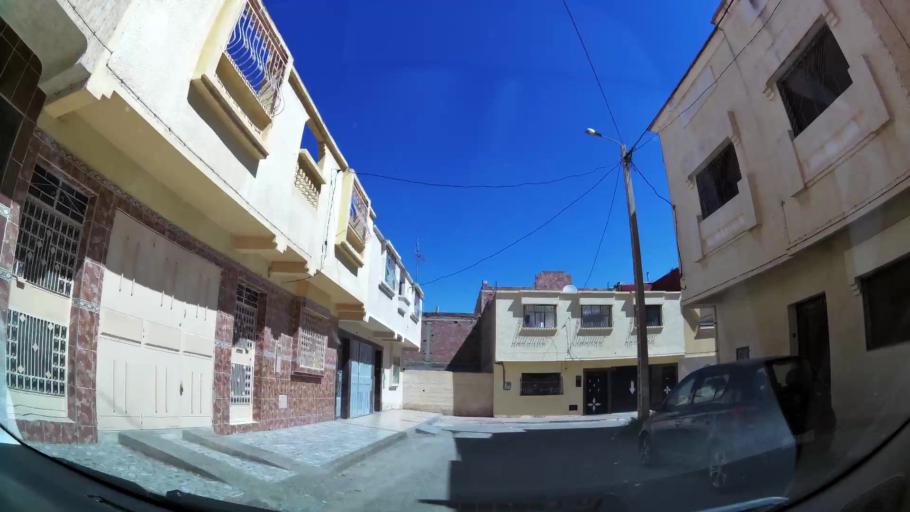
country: MA
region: Oriental
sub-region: Oujda-Angad
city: Oujda
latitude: 34.6640
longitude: -1.8894
